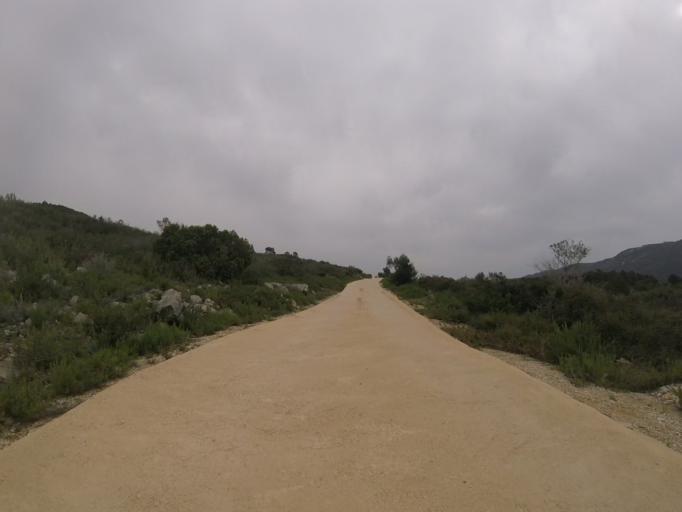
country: ES
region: Valencia
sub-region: Provincia de Castello
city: Alcala de Xivert
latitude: 40.2947
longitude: 0.2551
